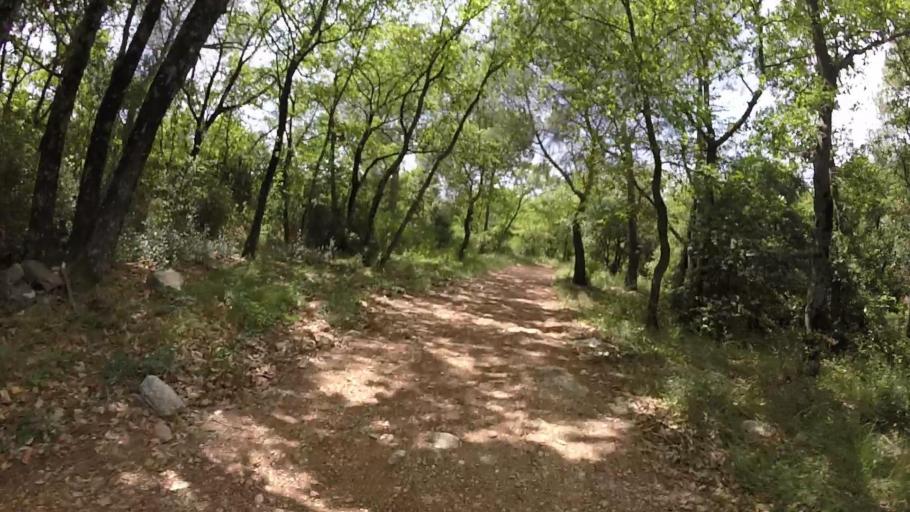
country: FR
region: Provence-Alpes-Cote d'Azur
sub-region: Departement des Alpes-Maritimes
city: Mougins
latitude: 43.6168
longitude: 7.0324
